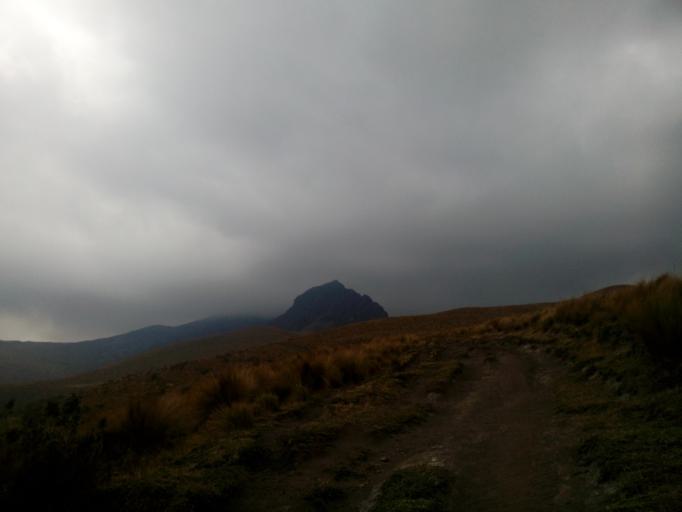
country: EC
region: Pichincha
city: Machachi
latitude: -0.5560
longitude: -78.5298
